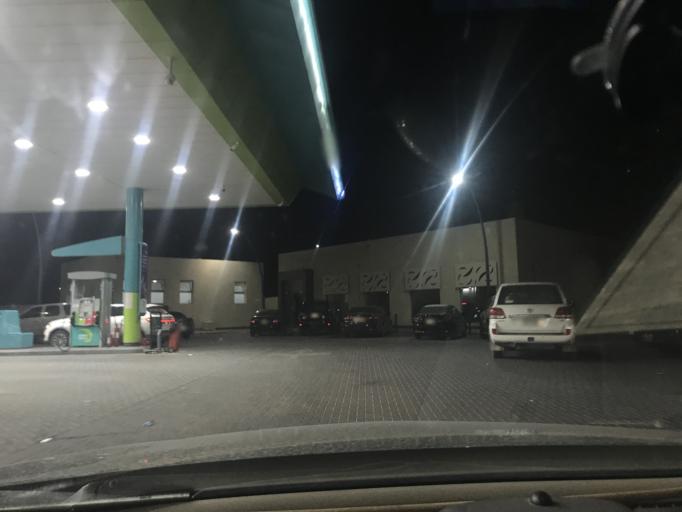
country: SA
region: Ar Riyad
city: Riyadh
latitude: 24.8466
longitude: 46.7337
